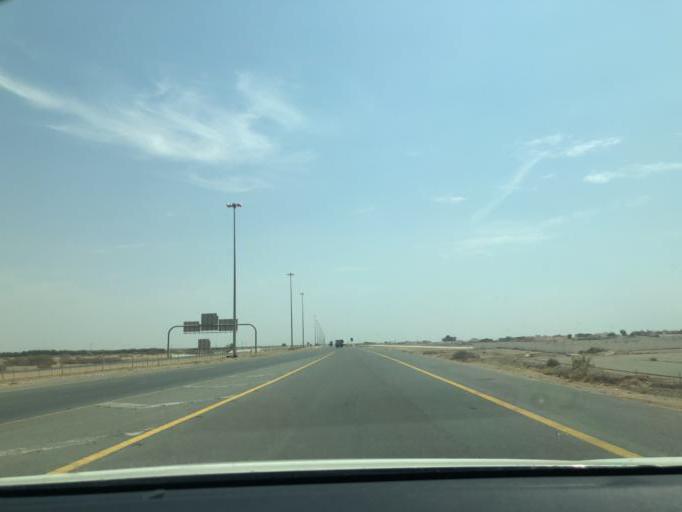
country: SA
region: Makkah
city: Rabigh
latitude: 22.2712
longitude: 39.1242
